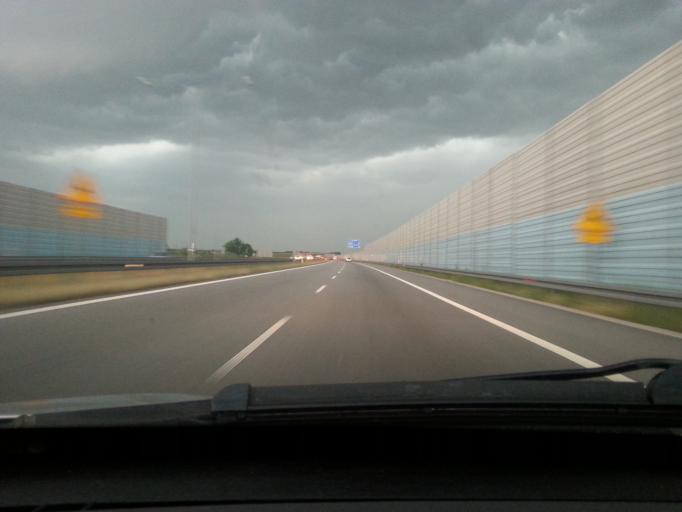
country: PL
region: Lodz Voivodeship
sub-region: powiat Lowicki
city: Lyszkowice
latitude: 51.9846
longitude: 19.8895
